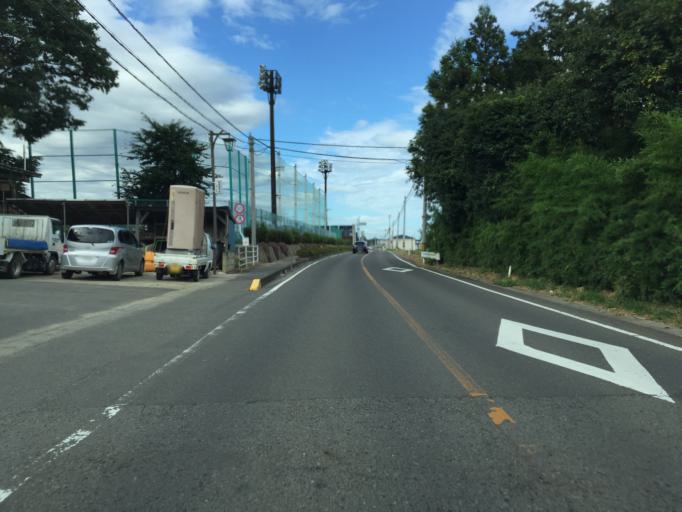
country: JP
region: Fukushima
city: Motomiya
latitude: 37.5354
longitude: 140.3720
